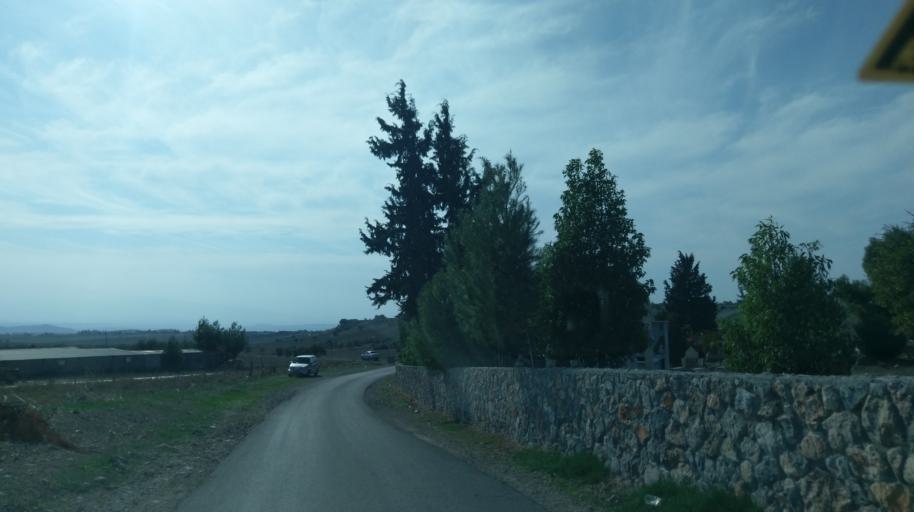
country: CY
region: Keryneia
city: Lapithos
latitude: 35.2834
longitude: 33.2356
